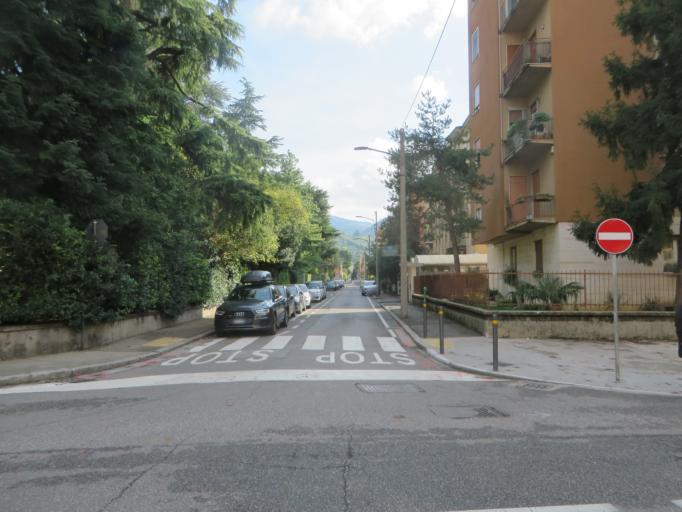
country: IT
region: Lombardy
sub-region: Provincia di Brescia
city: Brescia
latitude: 45.5520
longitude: 10.2182
